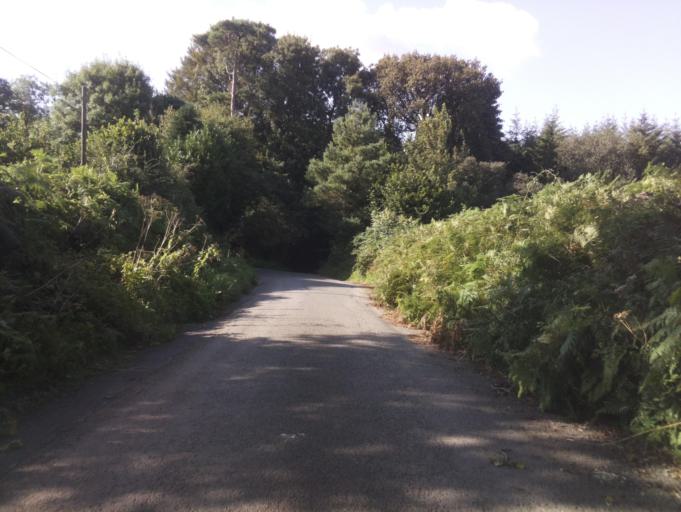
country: GB
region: England
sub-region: Devon
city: Buckfastleigh
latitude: 50.4399
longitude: -3.7847
